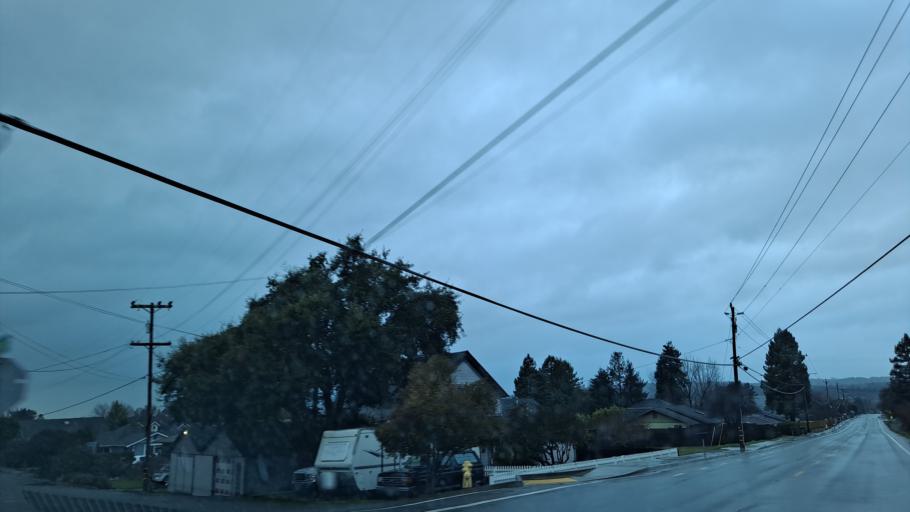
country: US
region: California
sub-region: Humboldt County
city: Fortuna
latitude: 40.5739
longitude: -124.1279
